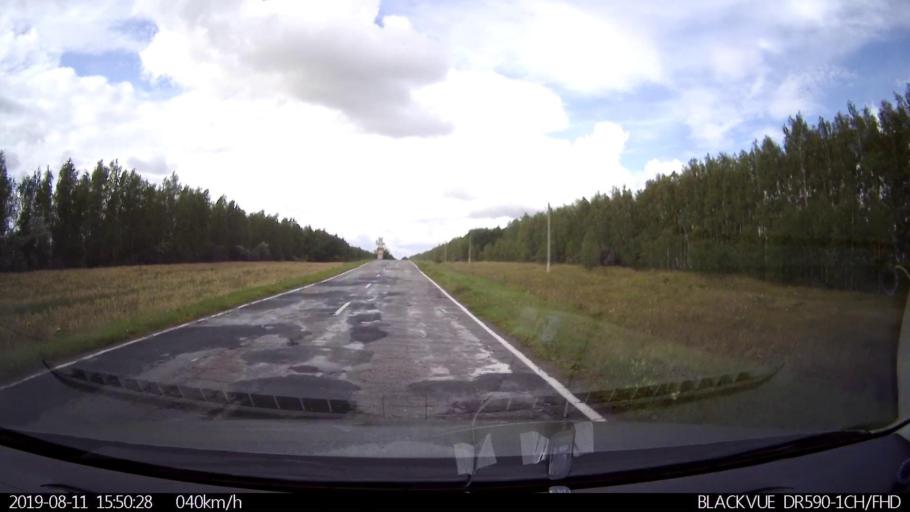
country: RU
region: Ulyanovsk
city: Ignatovka
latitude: 53.9120
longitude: 47.6558
